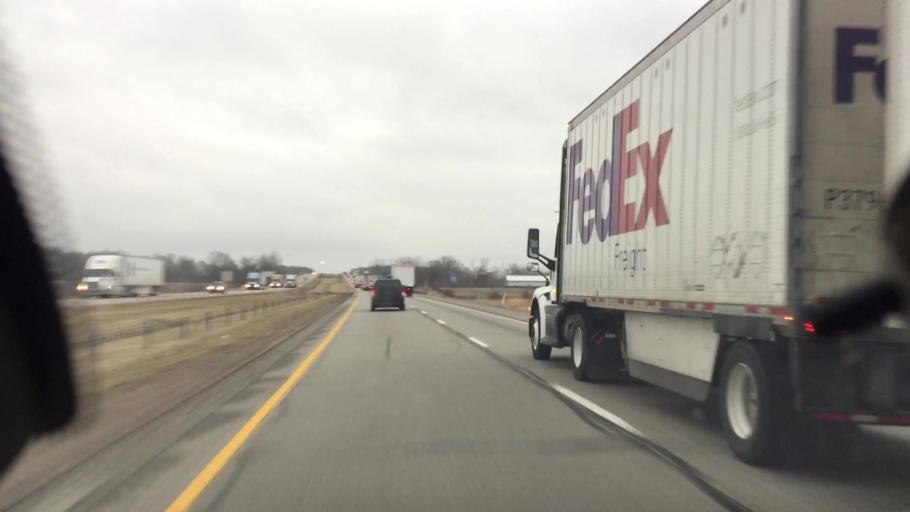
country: US
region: Indiana
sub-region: Wayne County
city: Cambridge City
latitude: 39.8534
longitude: -85.2474
